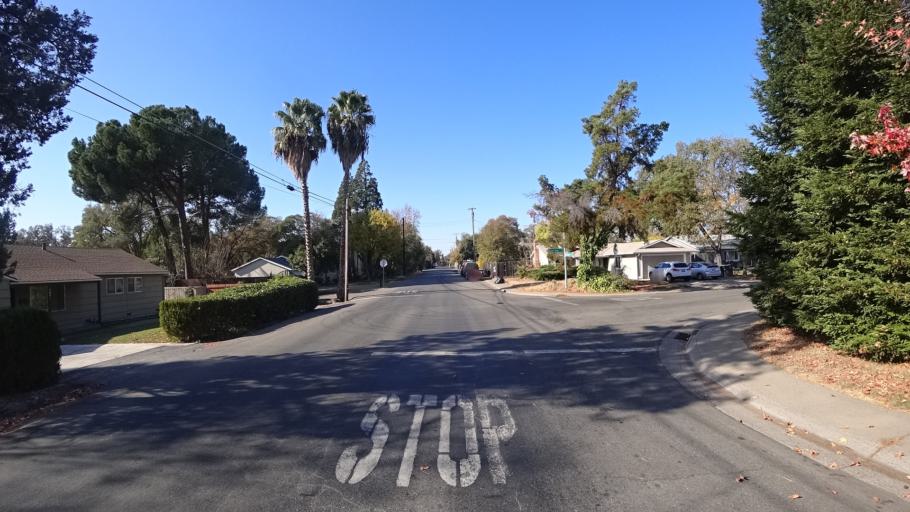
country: US
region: California
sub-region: Sacramento County
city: Citrus Heights
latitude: 38.6910
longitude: -121.2849
